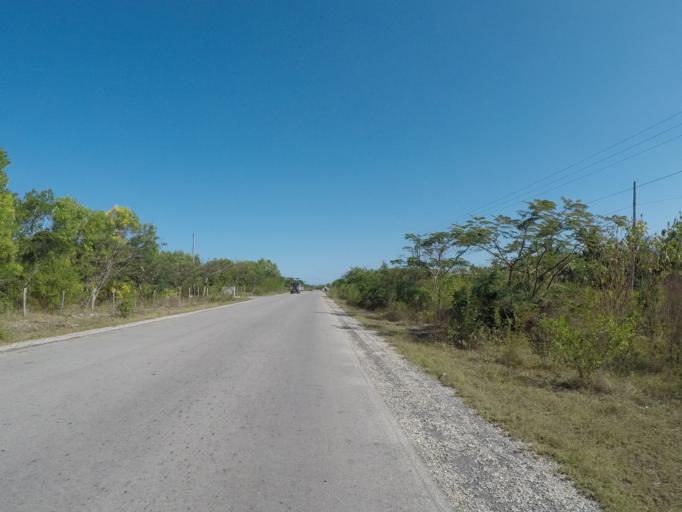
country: TZ
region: Zanzibar Central/South
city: Nganane
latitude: -6.1798
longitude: 39.5276
